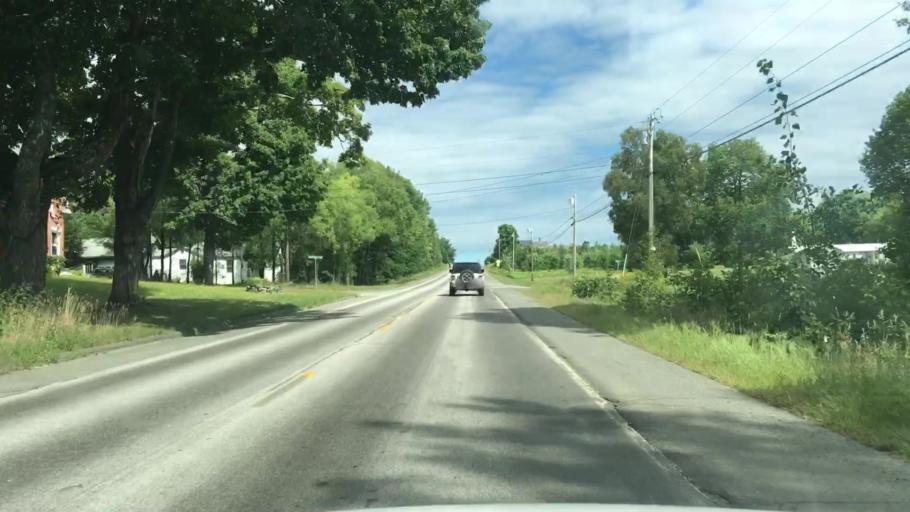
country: US
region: Maine
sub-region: Piscataquis County
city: Dover-Foxcroft
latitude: 45.1602
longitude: -69.2325
